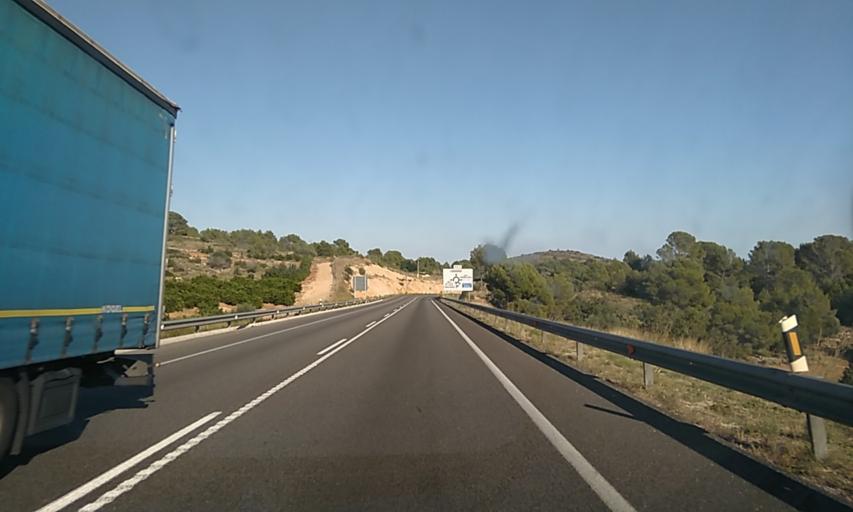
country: ES
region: Valencia
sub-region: Provincia de Castello
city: Torreblanca
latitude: 40.2319
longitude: 0.2034
